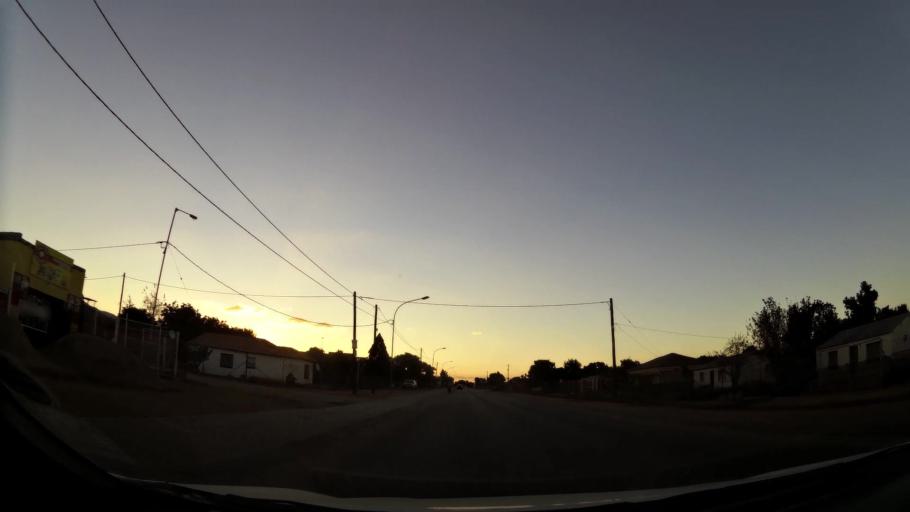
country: ZA
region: Limpopo
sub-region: Waterberg District Municipality
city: Mokopane
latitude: -24.1479
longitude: 28.9783
